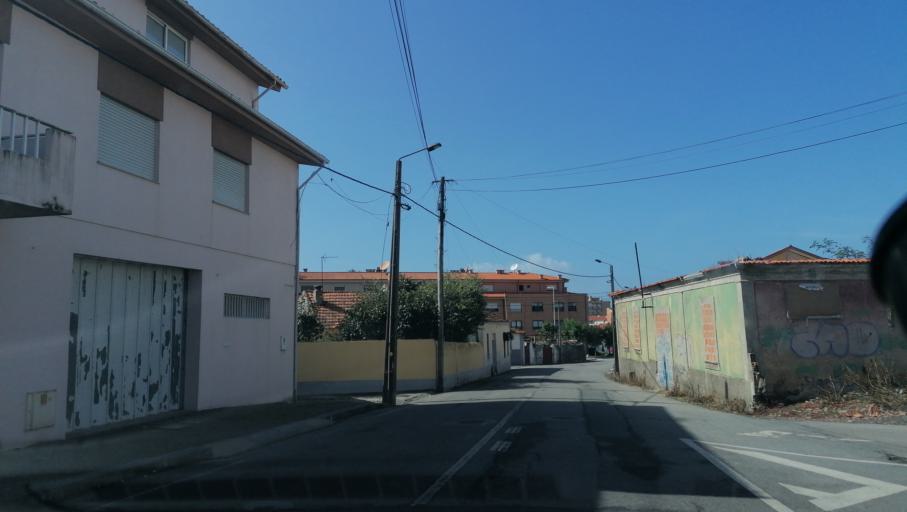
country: PT
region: Aveiro
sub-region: Espinho
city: Espinho
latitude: 41.0063
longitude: -8.6293
